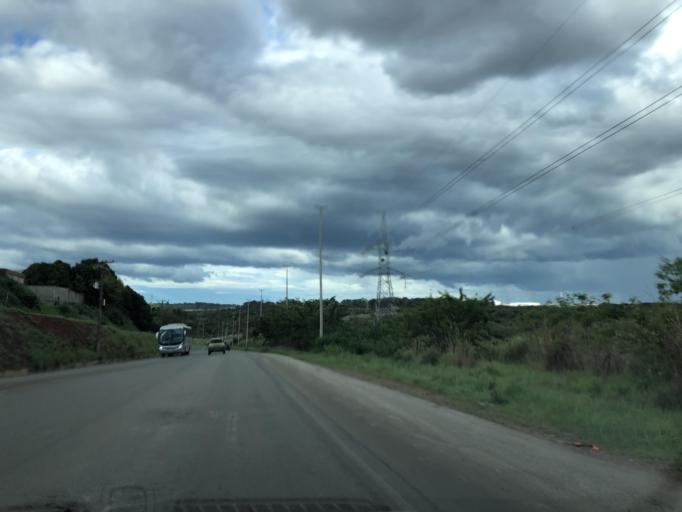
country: BR
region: Goias
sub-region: Luziania
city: Luziania
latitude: -16.0418
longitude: -48.0575
